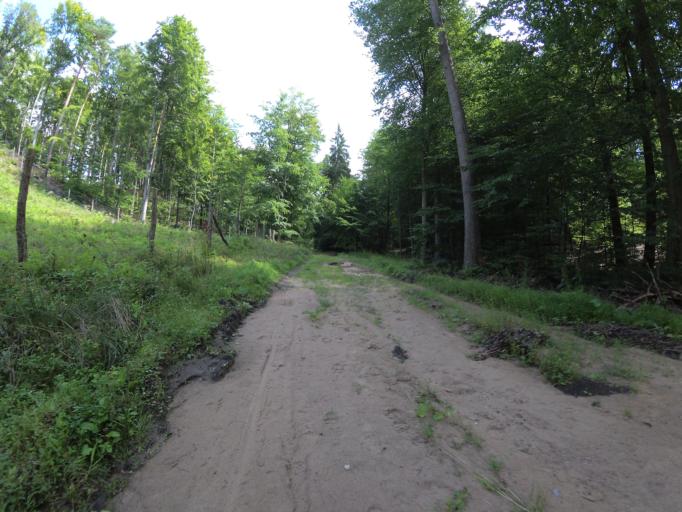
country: PL
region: Pomeranian Voivodeship
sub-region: Gdynia
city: Wielki Kack
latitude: 54.5102
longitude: 18.4737
